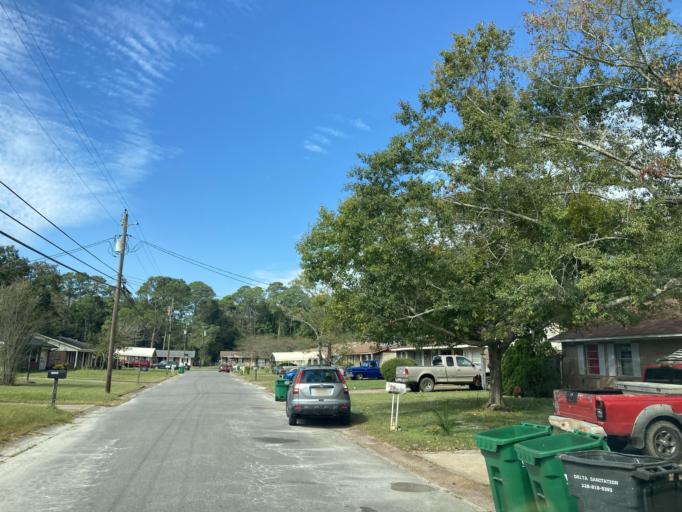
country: US
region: Mississippi
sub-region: Jackson County
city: Saint Martin
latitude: 30.4472
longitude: -88.8743
